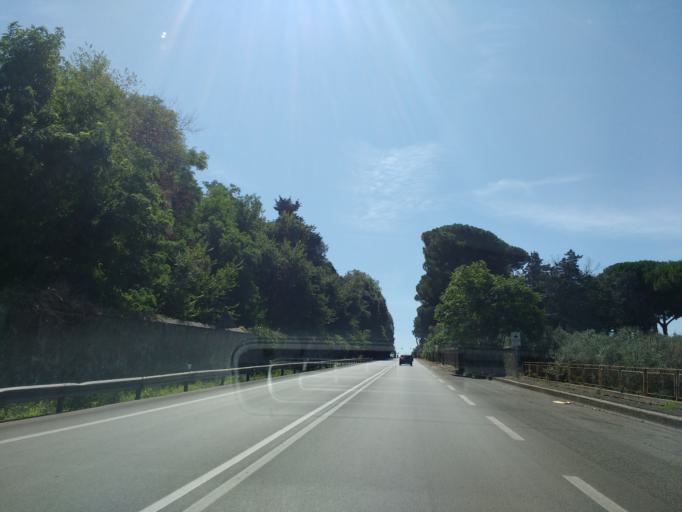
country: IT
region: Latium
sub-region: Citta metropolitana di Roma Capitale
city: Castel Gandolfo
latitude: 41.7449
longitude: 12.6406
